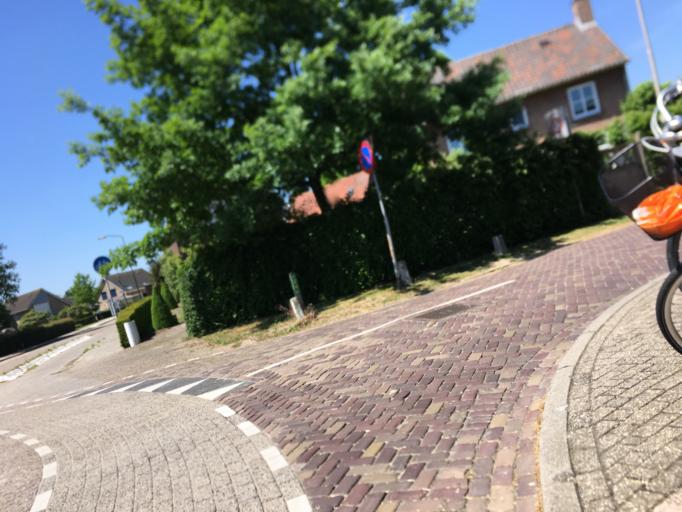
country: NL
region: North Brabant
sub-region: Gemeente Heusden
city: Heusden
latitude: 51.7318
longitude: 5.1577
